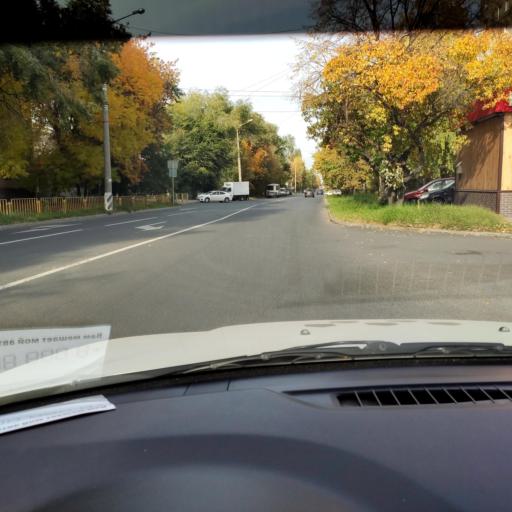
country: RU
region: Samara
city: Tol'yatti
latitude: 53.5214
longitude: 49.4268
